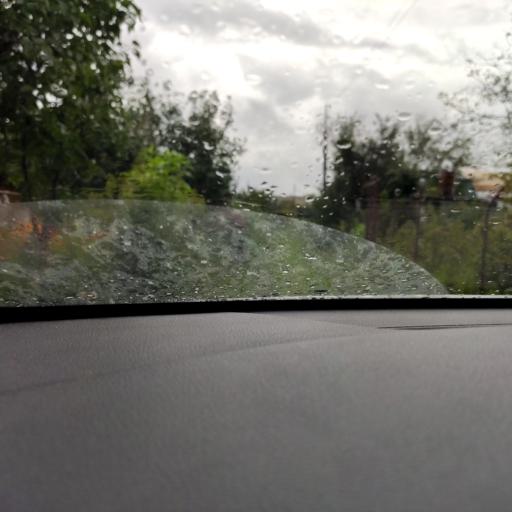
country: RU
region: Tatarstan
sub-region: Gorod Kazan'
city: Kazan
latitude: 55.8321
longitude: 49.2030
